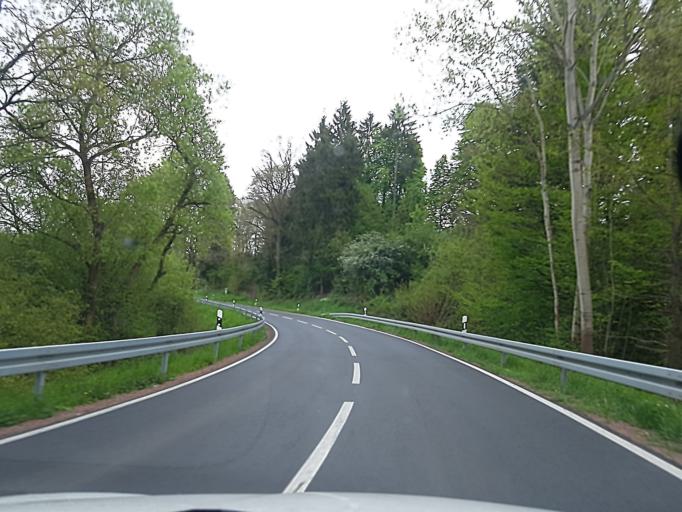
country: DE
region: Hesse
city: Bad Camberg
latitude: 50.2634
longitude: 8.2389
